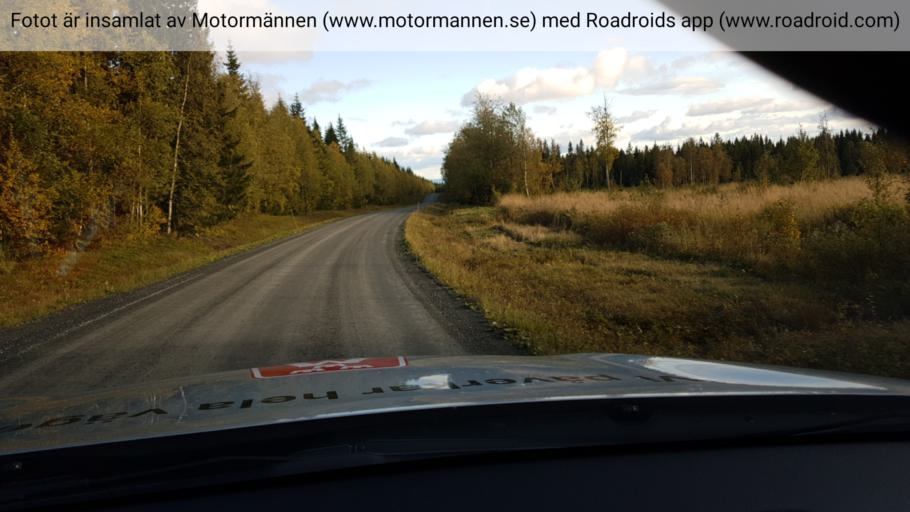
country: SE
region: Jaemtland
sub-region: Krokoms Kommun
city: Krokom
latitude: 63.7582
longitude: 14.4356
